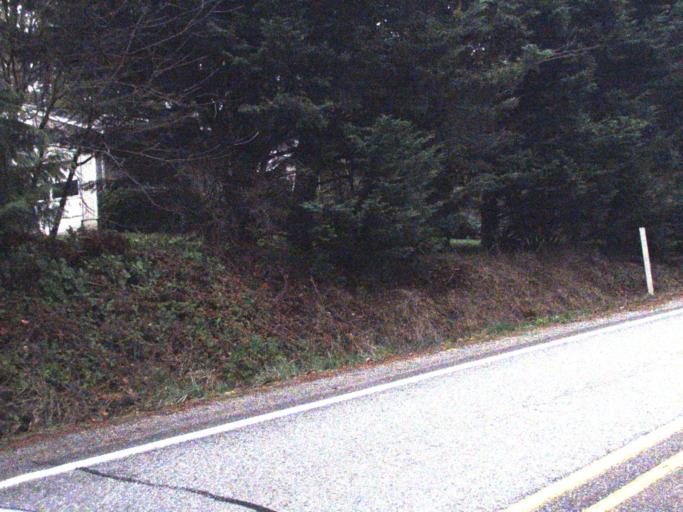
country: US
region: Washington
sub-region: Snohomish County
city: Warm Beach
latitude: 48.1565
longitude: -122.2797
